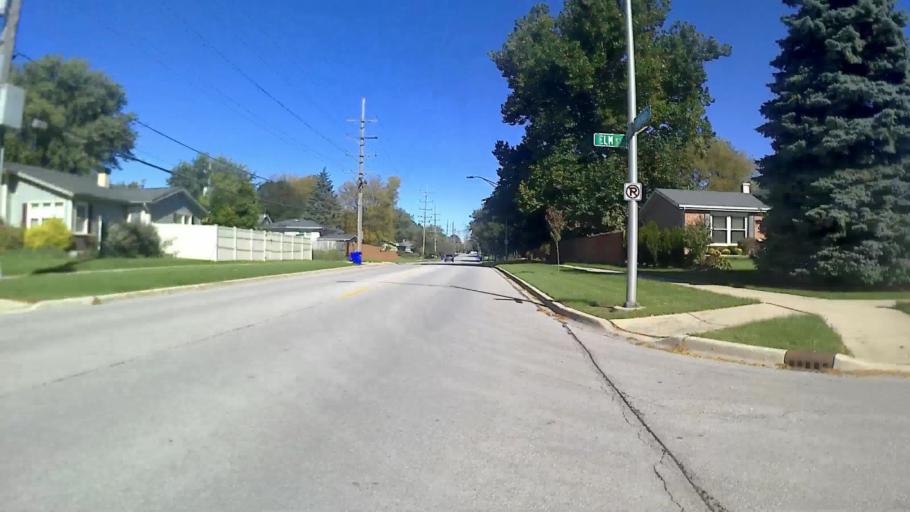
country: US
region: Illinois
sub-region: DuPage County
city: Wheaton
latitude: 41.8553
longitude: -88.0870
